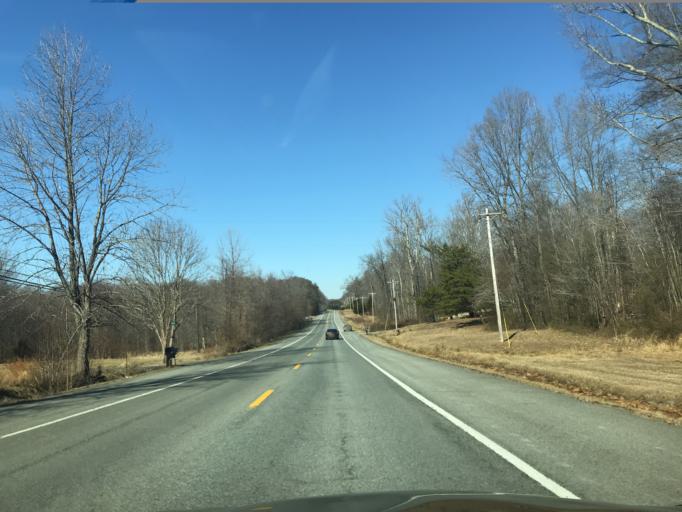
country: US
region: Maryland
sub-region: Charles County
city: Bryans Road
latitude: 38.6524
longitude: -77.0764
